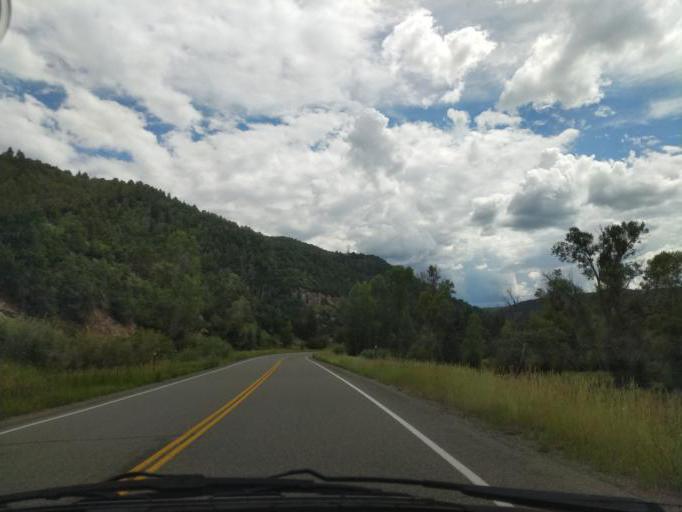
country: US
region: Colorado
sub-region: Delta County
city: Paonia
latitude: 39.0429
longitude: -107.3608
